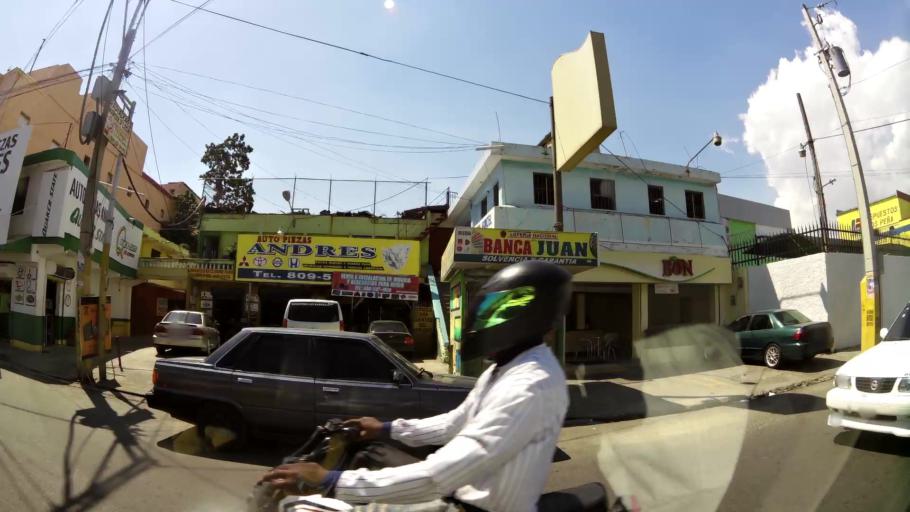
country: DO
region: Nacional
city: Bella Vista
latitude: 18.4626
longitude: -69.9758
